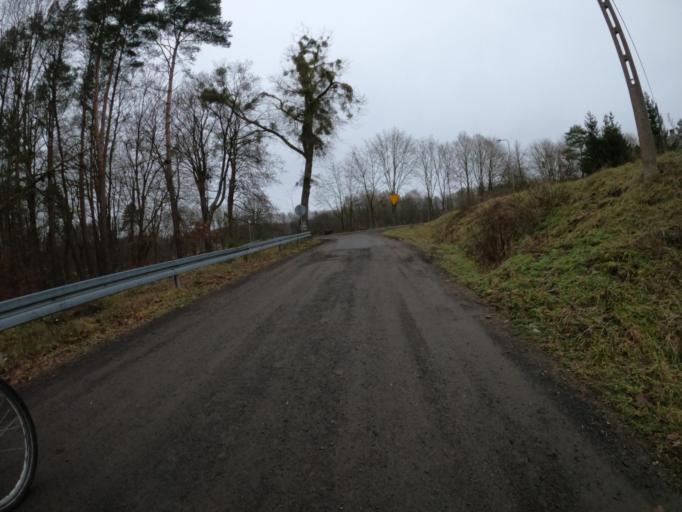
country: PL
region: West Pomeranian Voivodeship
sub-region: Powiat mysliborski
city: Debno
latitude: 52.7435
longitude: 14.7699
